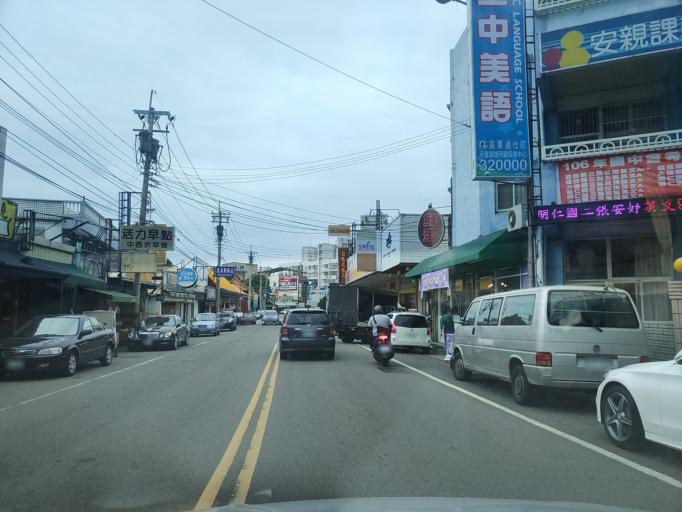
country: TW
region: Taiwan
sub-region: Miaoli
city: Miaoli
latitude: 24.5635
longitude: 120.8262
